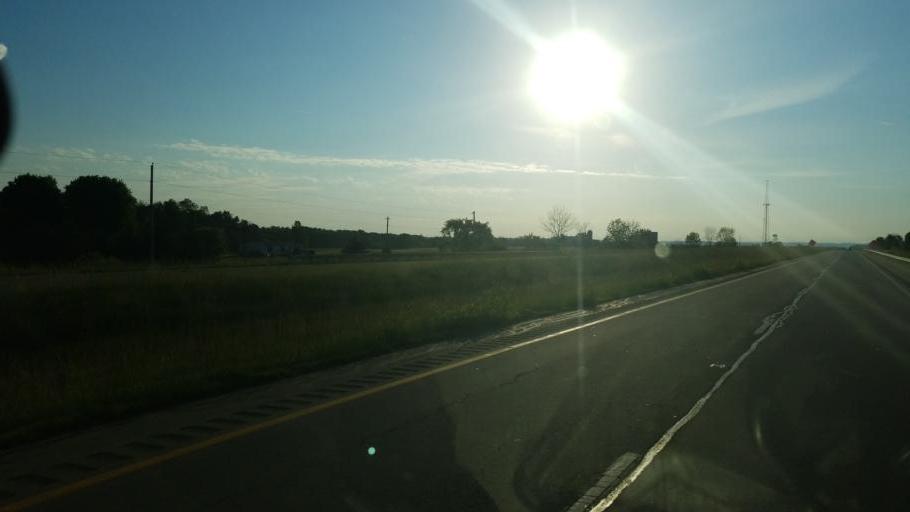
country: US
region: Ohio
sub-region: Ashland County
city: Ashland
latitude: 40.7846
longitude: -82.2986
